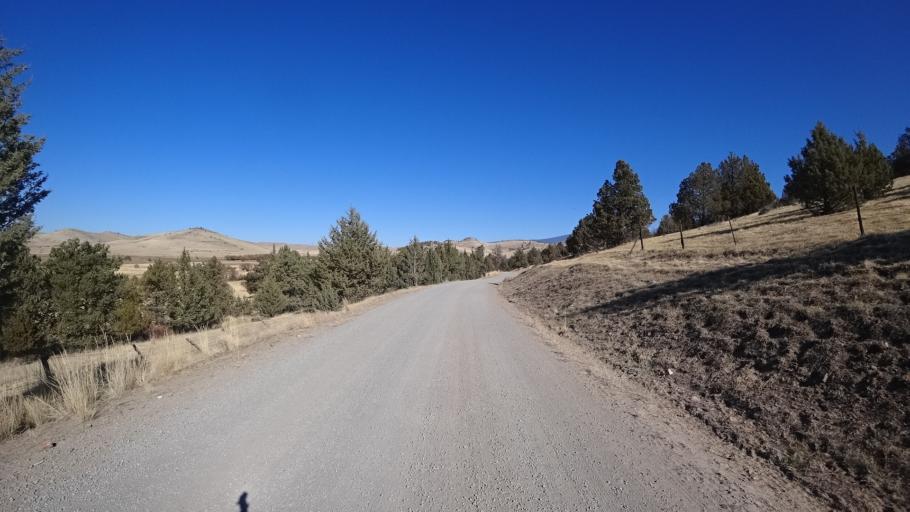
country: US
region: California
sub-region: Siskiyou County
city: Montague
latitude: 41.7192
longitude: -122.3720
